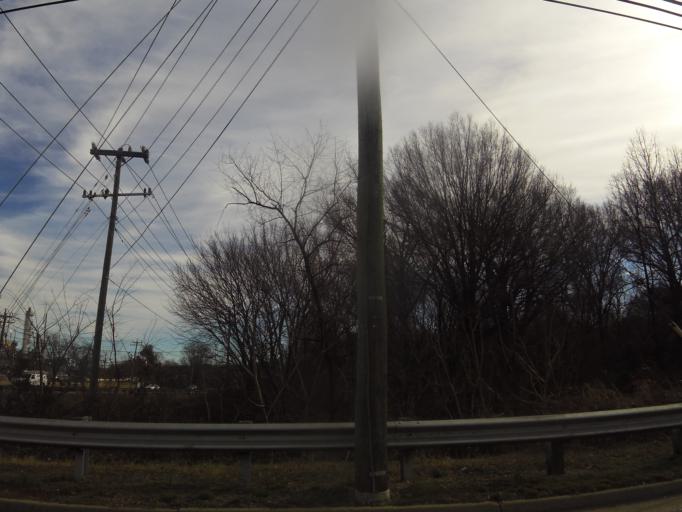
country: US
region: Virginia
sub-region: City of Hopewell
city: Hopewell
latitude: 37.2977
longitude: -77.2784
